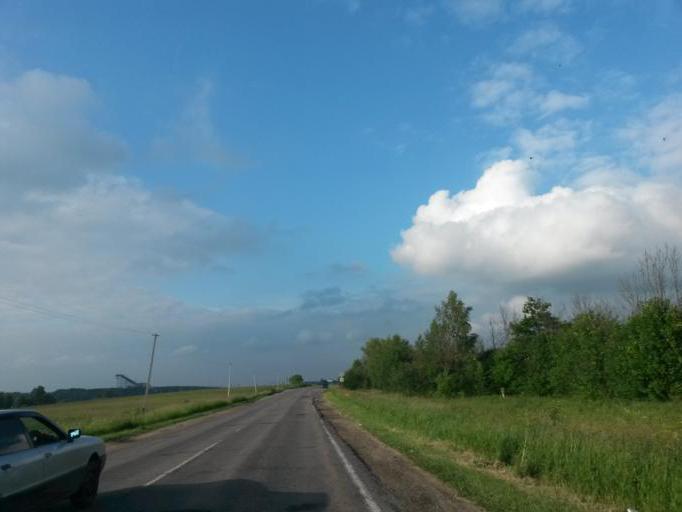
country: RU
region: Moskovskaya
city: Lyubuchany
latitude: 55.2508
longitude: 37.5930
